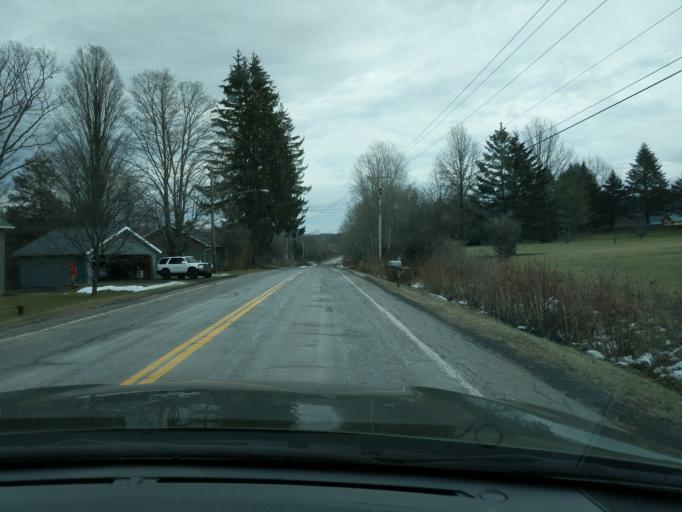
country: US
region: New York
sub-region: Tompkins County
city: East Ithaca
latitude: 42.3859
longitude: -76.3689
